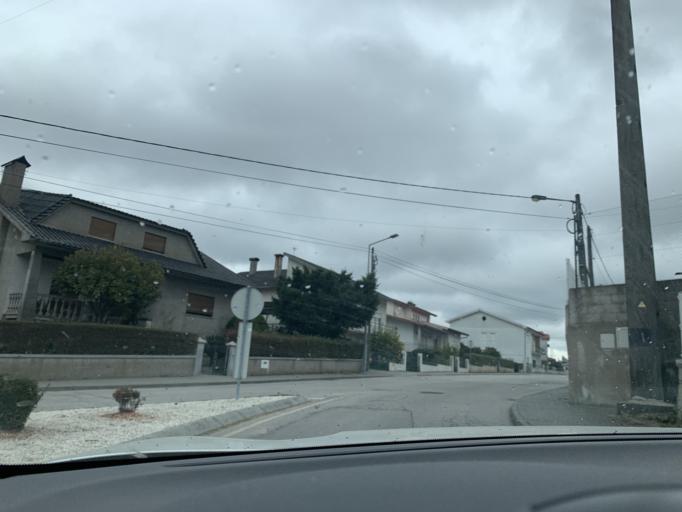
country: PT
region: Viseu
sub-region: Mangualde
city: Mangualde
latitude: 40.6122
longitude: -7.7671
